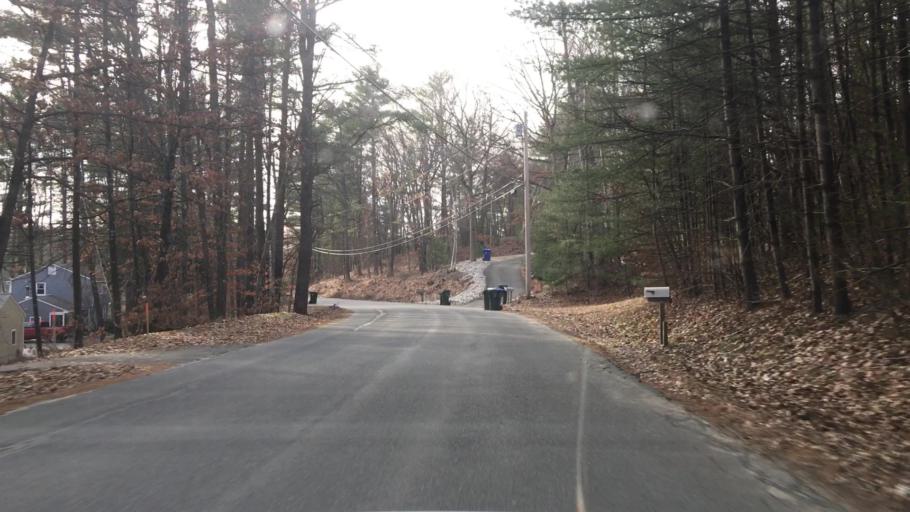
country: US
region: New Hampshire
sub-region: Rockingham County
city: Londonderry
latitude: 42.8852
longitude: -71.4162
